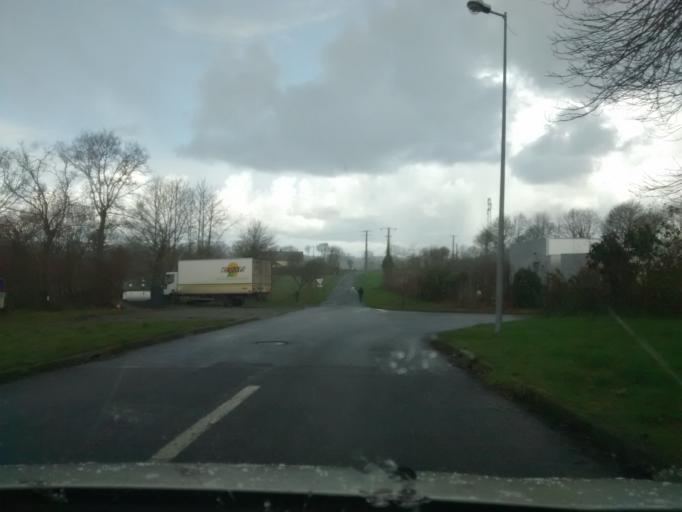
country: FR
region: Brittany
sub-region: Departement d'Ille-et-Vilaine
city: Fouillard
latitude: 48.1401
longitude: -1.5619
